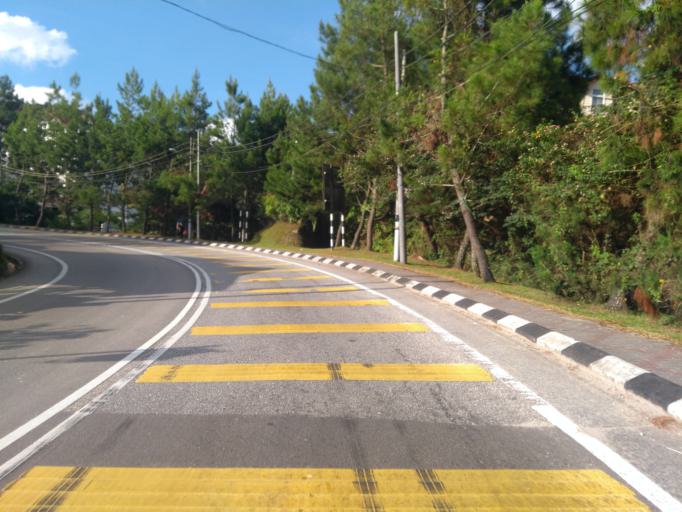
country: MY
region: Pahang
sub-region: Cameron Highlands
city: Tanah Rata
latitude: 4.4720
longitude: 101.3805
